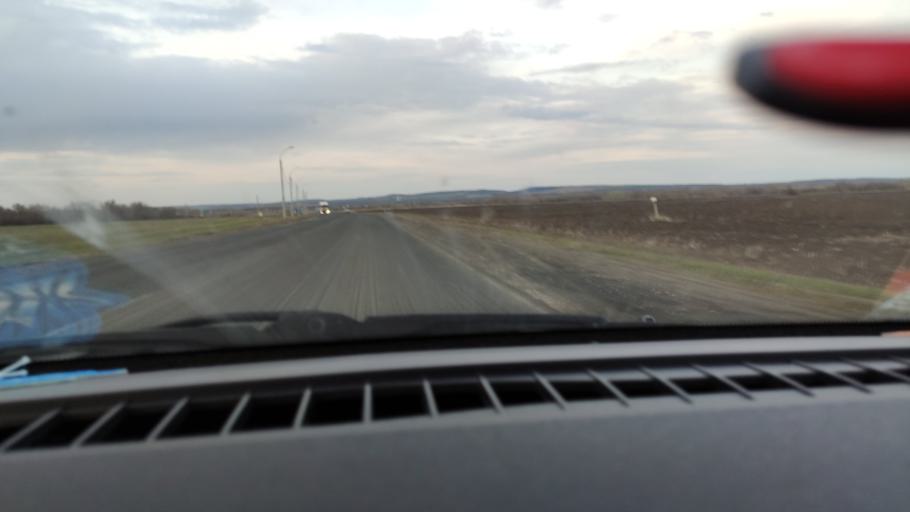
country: RU
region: Saratov
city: Yelshanka
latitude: 51.8152
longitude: 46.2092
